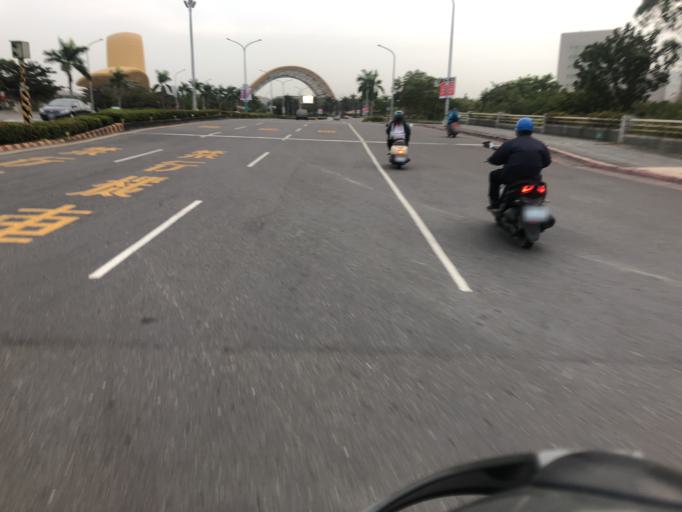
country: TW
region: Taiwan
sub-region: Tainan
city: Tainan
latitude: 23.0906
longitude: 120.2824
